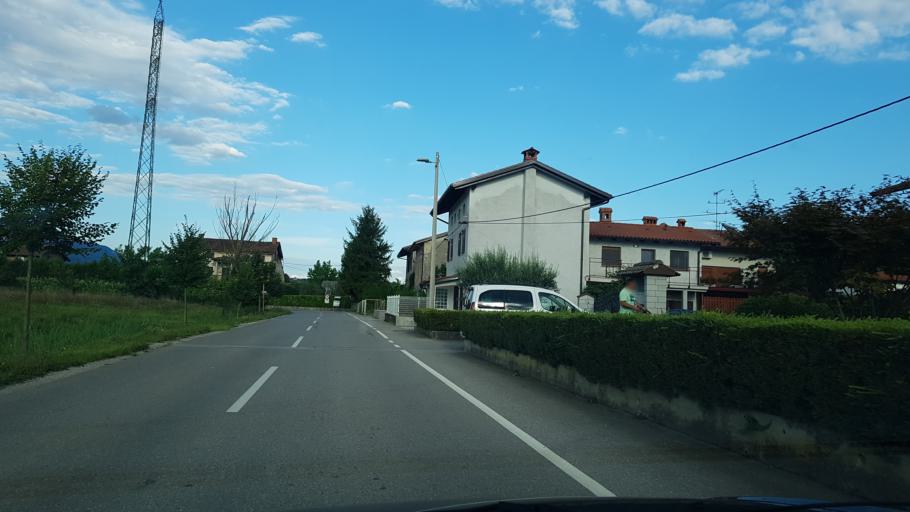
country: SI
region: Rence-Vogrsko
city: Rence
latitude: 45.8876
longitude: 13.6664
